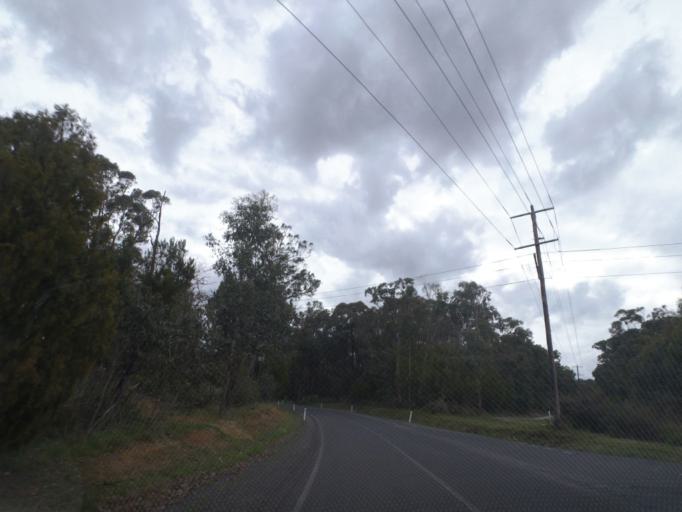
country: AU
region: Victoria
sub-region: Yarra Ranges
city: Mount Evelyn
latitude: -37.7677
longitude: 145.4141
